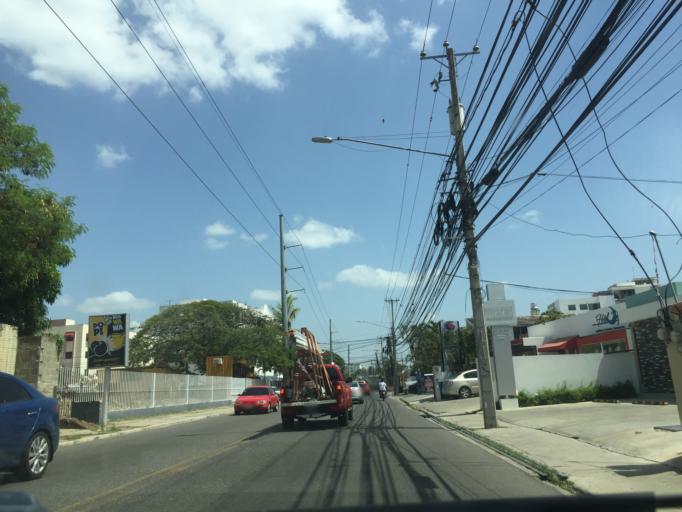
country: DO
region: Santiago
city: Santiago de los Caballeros
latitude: 19.4526
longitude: -70.6656
